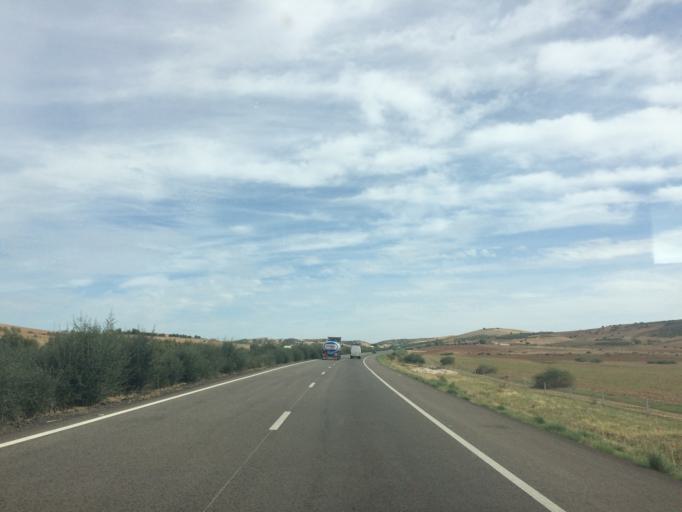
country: MA
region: Rabat-Sale-Zemmour-Zaer
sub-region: Khemisset
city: Khemisset
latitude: 33.8018
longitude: -5.8771
